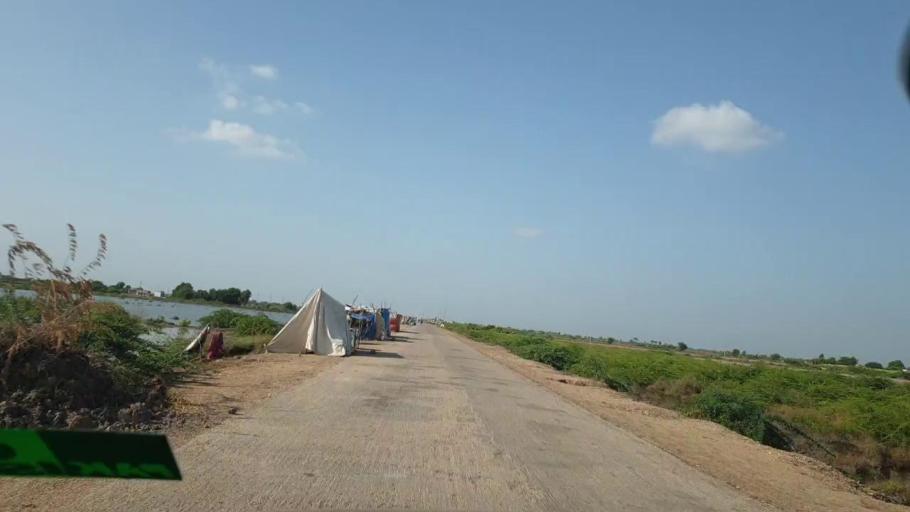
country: PK
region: Sindh
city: Naukot
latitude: 24.7376
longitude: 69.1984
